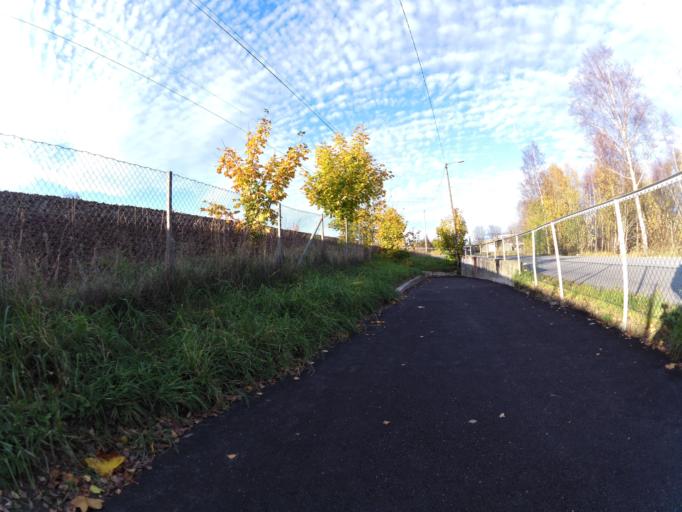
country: NO
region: Ostfold
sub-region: Fredrikstad
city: Fredrikstad
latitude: 59.2301
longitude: 10.9791
